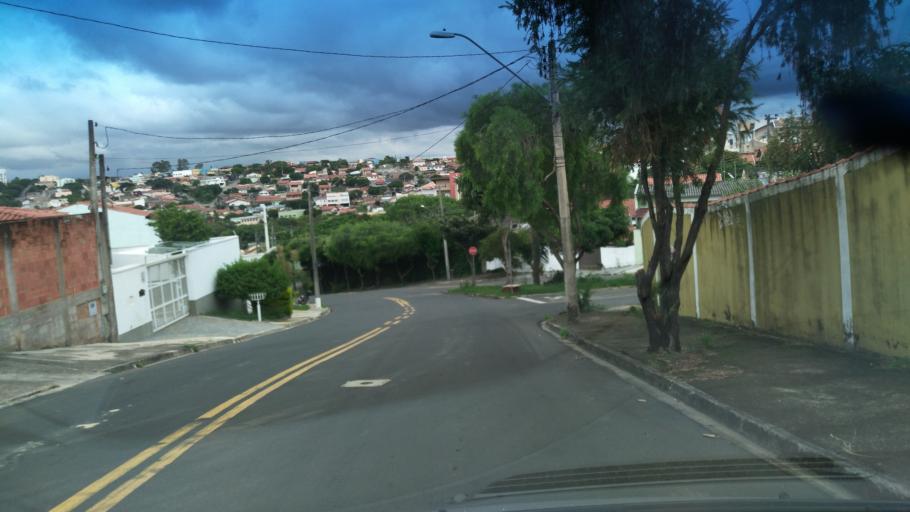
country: BR
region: Sao Paulo
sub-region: Valinhos
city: Valinhos
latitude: -22.9586
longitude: -46.9756
